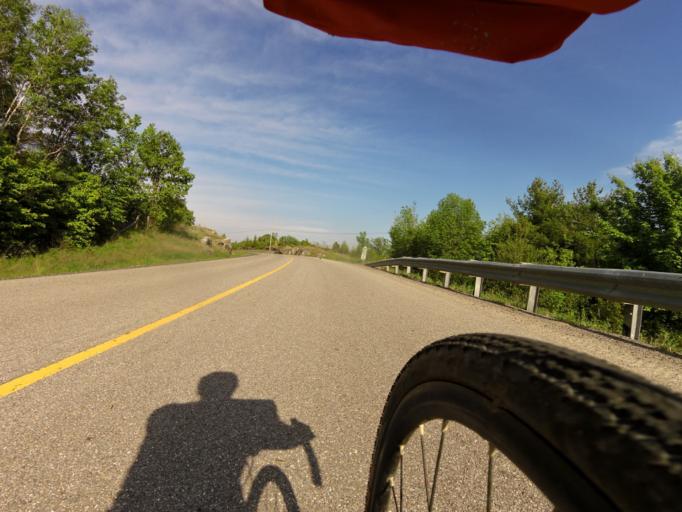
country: CA
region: Ontario
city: Arnprior
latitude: 45.1665
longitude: -76.4828
